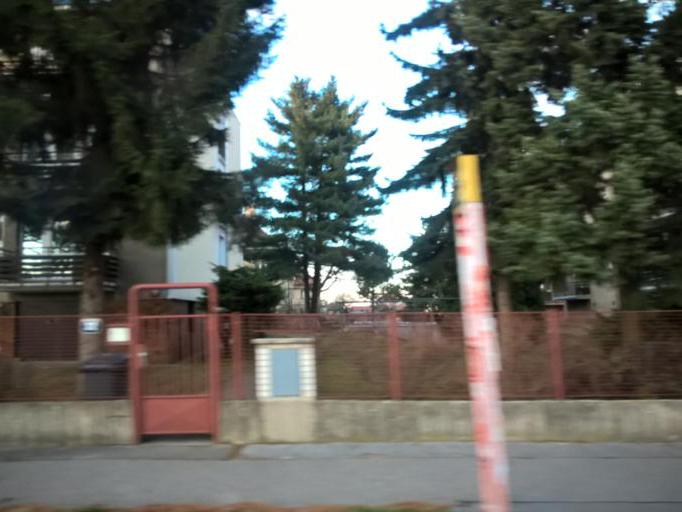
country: CZ
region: Praha
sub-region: Praha 1
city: Mala Strana
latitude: 50.0801
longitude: 14.3677
